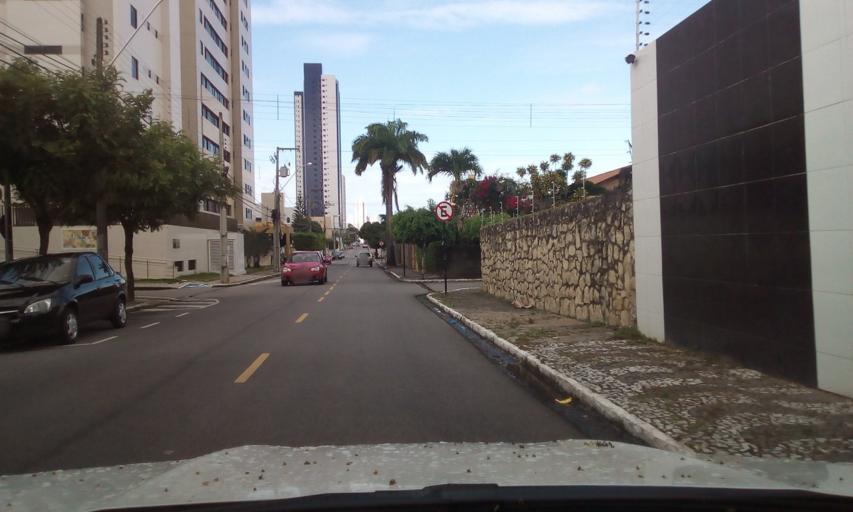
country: BR
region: Paraiba
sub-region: Joao Pessoa
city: Joao Pessoa
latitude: -7.1156
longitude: -34.8582
